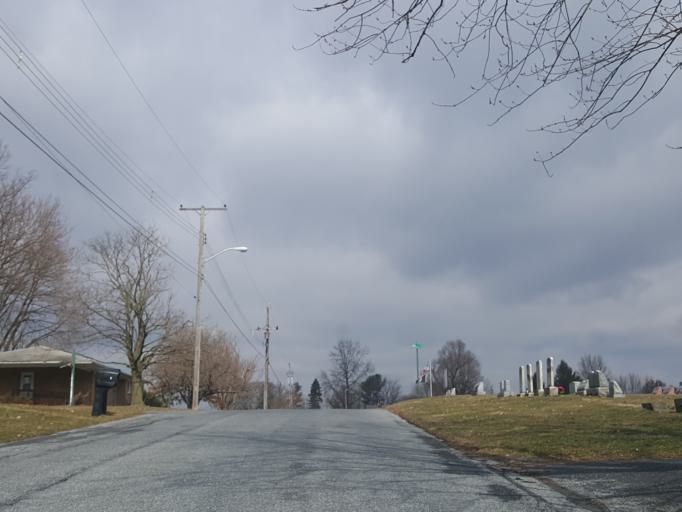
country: US
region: Pennsylvania
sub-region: Lebanon County
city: Jonestown
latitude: 40.4165
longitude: -76.4770
